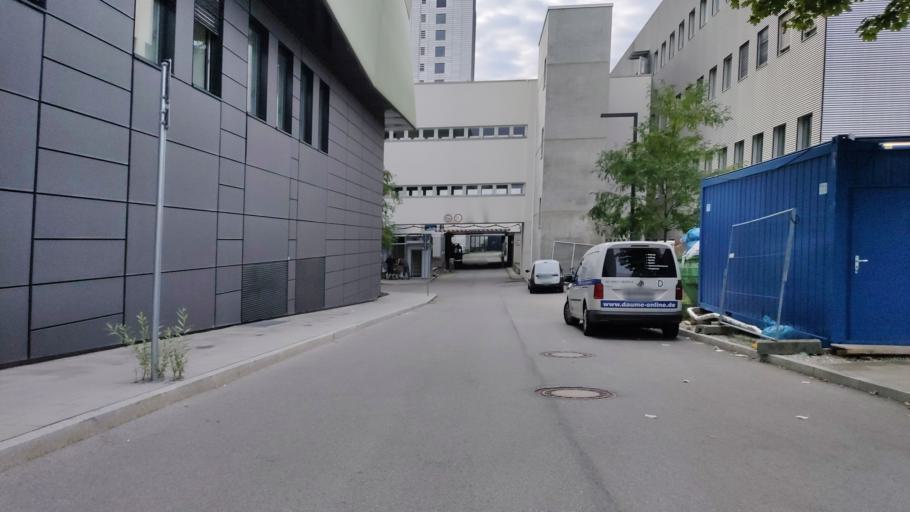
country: DE
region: Bavaria
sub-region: Upper Bavaria
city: Neuried
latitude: 48.1121
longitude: 11.4676
